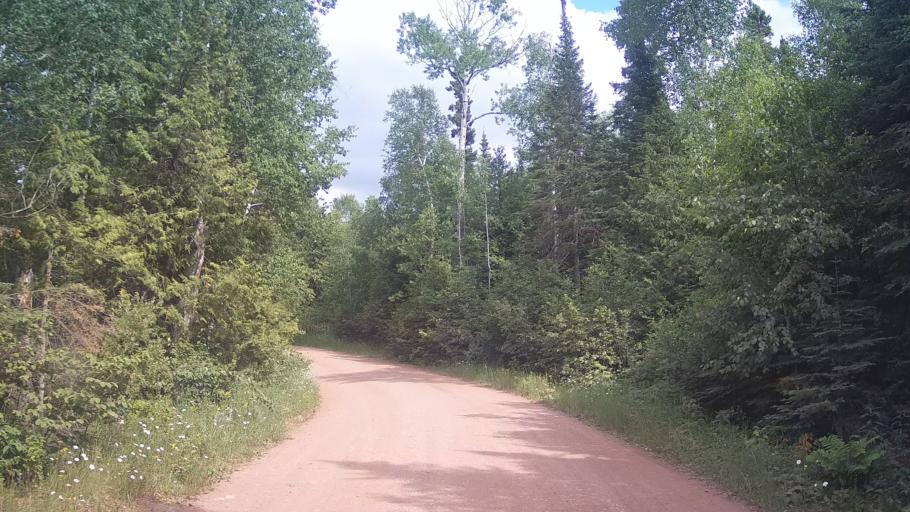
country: CA
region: Ontario
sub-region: Thunder Bay District
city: Thunder Bay
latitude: 48.6711
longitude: -88.6678
